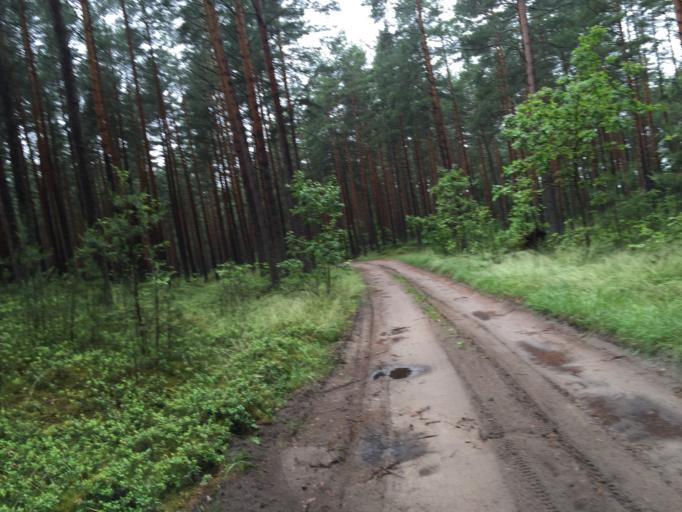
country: LV
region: Riga
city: Jaunciems
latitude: 57.0728
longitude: 24.1488
